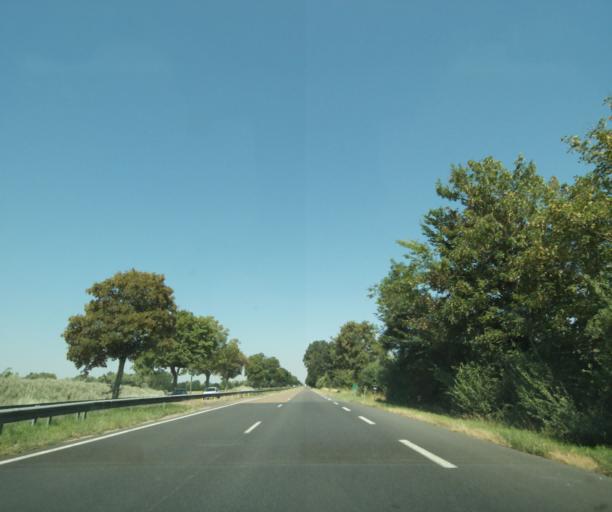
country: FR
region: Champagne-Ardenne
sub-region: Departement de la Marne
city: Pargny-sur-Saulx
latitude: 48.6693
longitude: 4.7817
